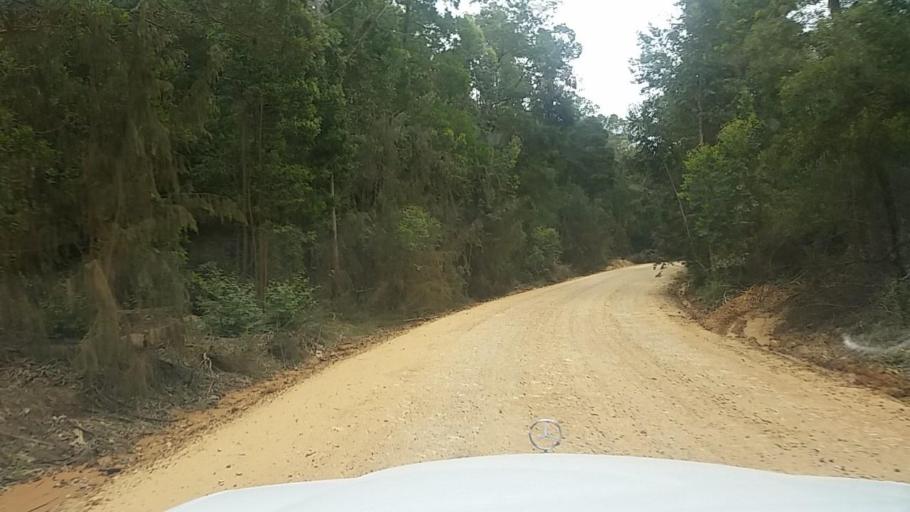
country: ZA
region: Western Cape
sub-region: Eden District Municipality
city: Knysna
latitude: -33.9977
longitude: 23.1233
